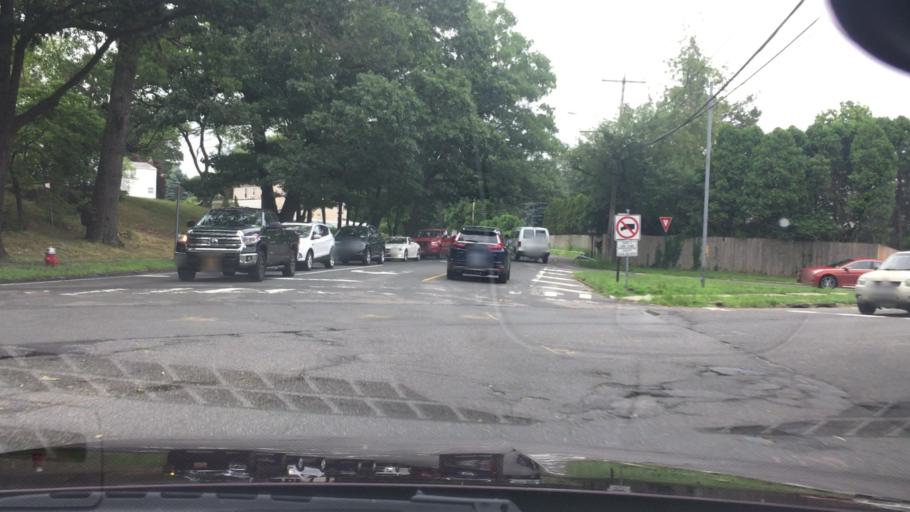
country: US
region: New York
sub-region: Suffolk County
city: South Huntington
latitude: 40.8136
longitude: -73.4078
